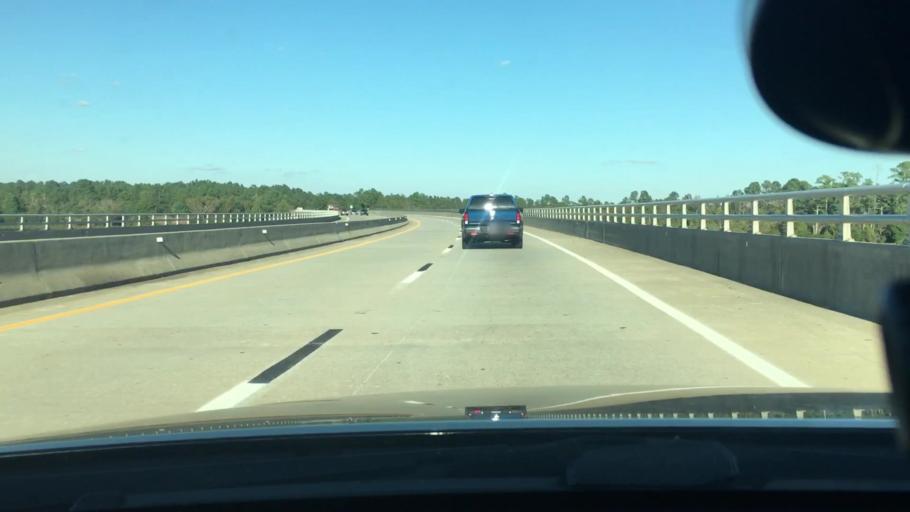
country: US
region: North Carolina
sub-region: Craven County
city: James City
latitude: 35.1006
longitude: -77.0132
